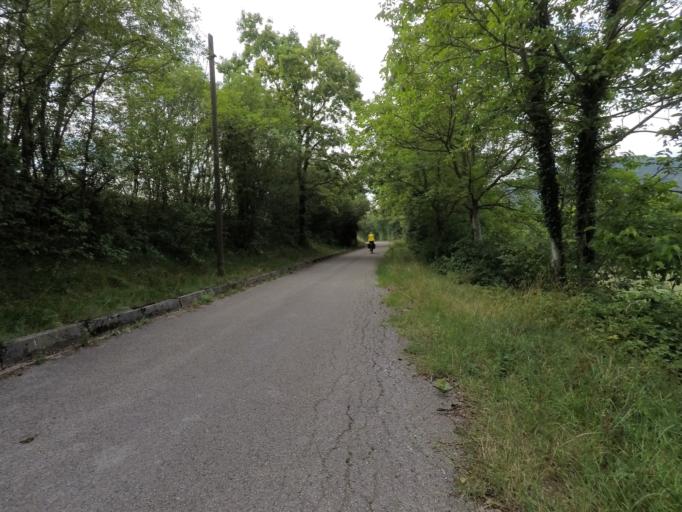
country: IT
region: Friuli Venezia Giulia
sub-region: Provincia di Pordenone
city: Travesio
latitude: 46.1895
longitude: 12.8744
